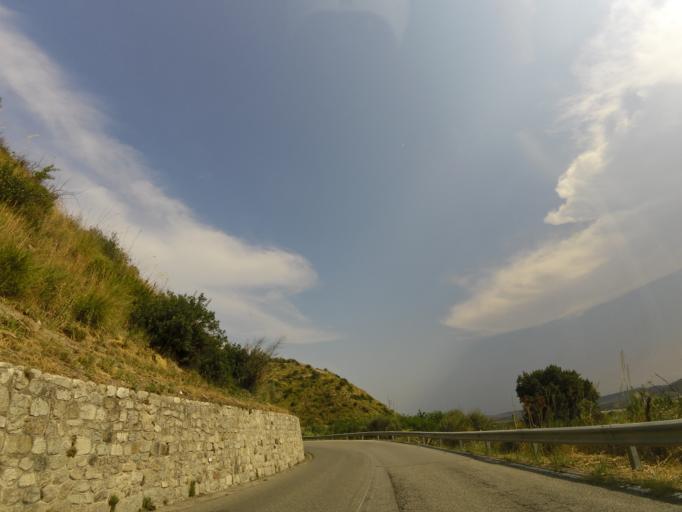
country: IT
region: Calabria
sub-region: Provincia di Reggio Calabria
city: Monasterace
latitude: 38.4592
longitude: 16.5223
